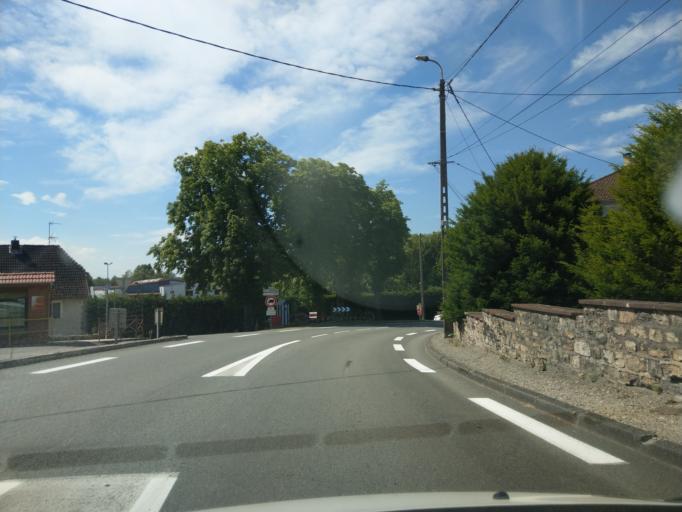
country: FR
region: Franche-Comte
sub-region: Territoire de Belfort
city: Offemont
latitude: 47.6694
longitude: 6.9189
